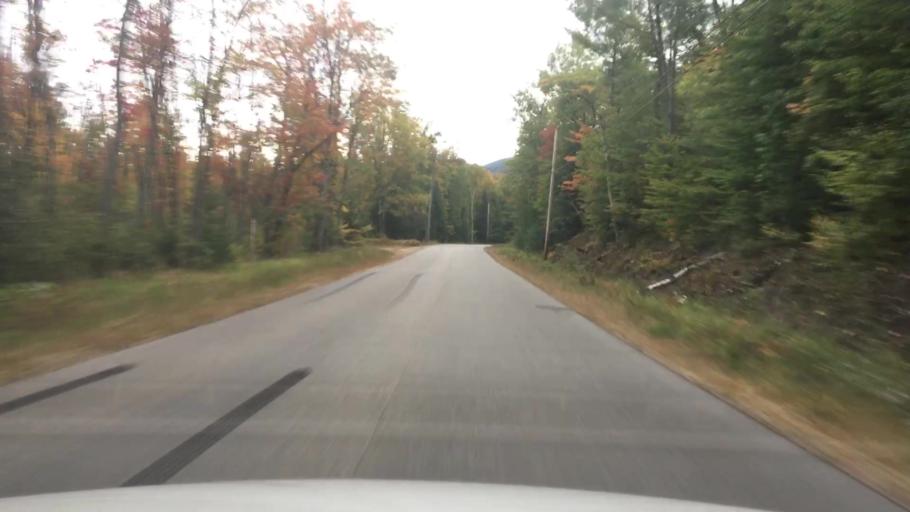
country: US
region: Maine
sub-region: Oxford County
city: Bethel
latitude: 44.4779
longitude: -70.7837
